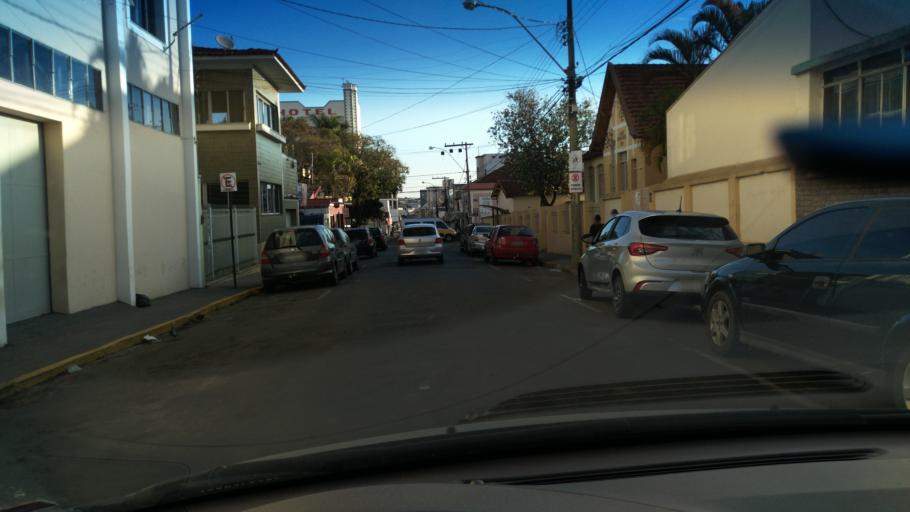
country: BR
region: Minas Gerais
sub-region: Andradas
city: Andradas
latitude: -22.0706
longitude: -46.5728
